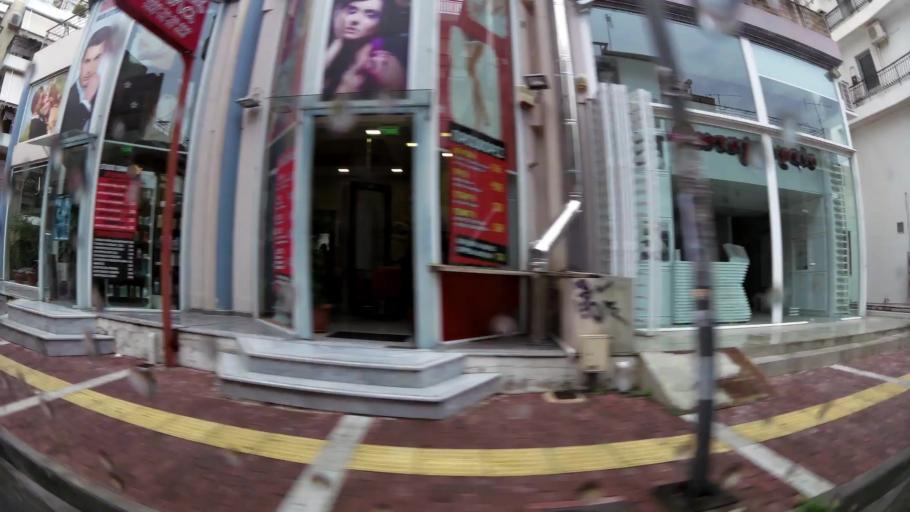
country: GR
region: Attica
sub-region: Nomarchia Athinas
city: Ymittos
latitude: 37.9560
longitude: 23.7529
